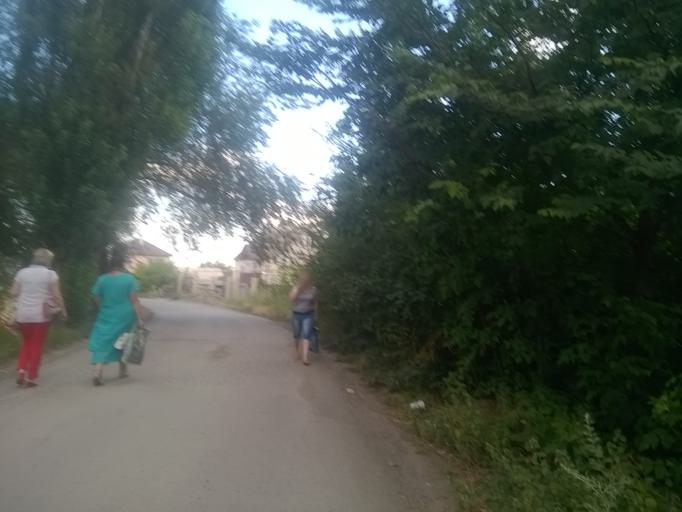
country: RU
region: Rostov
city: Donetsk
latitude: 48.3375
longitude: 39.9552
